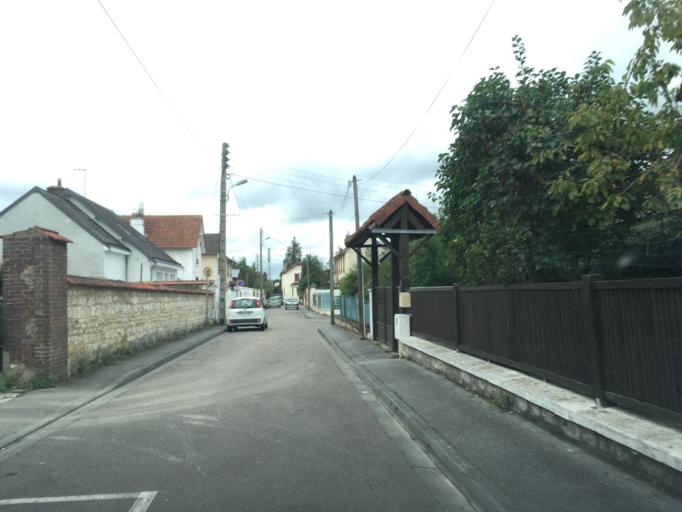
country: FR
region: Haute-Normandie
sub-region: Departement de l'Eure
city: Vernon
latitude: 49.0913
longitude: 1.4750
